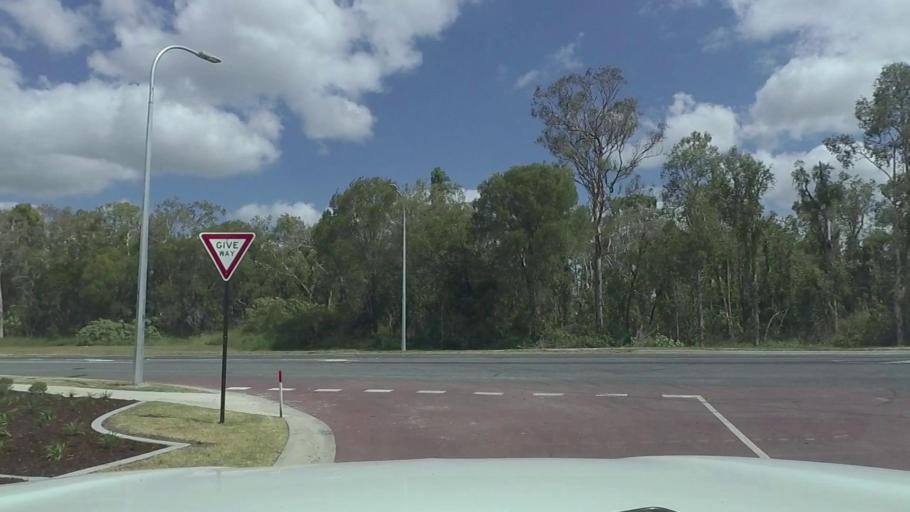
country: AU
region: Queensland
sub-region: Logan
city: Logan Reserve
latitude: -27.7209
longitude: 153.0883
